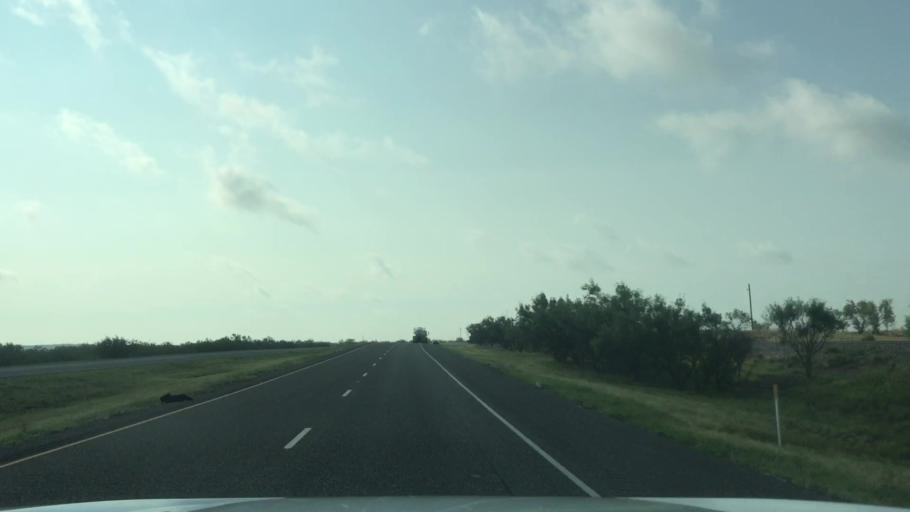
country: US
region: Texas
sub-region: Scurry County
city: Snyder
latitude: 32.8348
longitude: -100.9894
